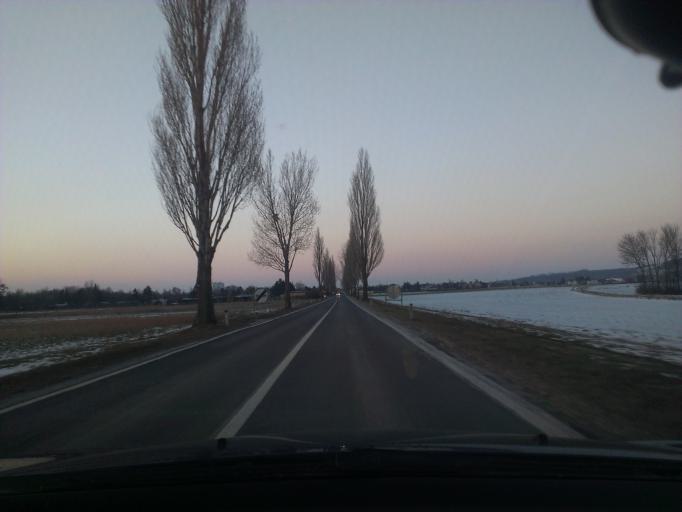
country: AT
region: Lower Austria
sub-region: Politischer Bezirk Bruck an der Leitha
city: Enzersdorf an der Fischa
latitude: 48.0713
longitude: 16.6091
